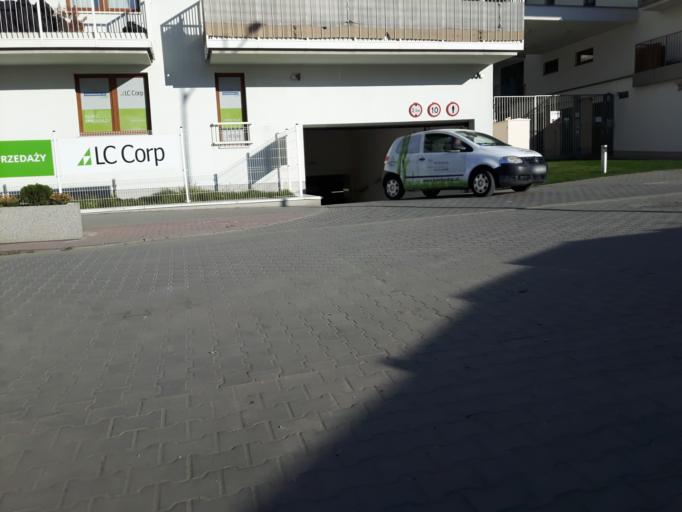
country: PL
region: Masovian Voivodeship
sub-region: Powiat wolominski
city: Zabki
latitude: 52.2806
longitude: 21.1338
